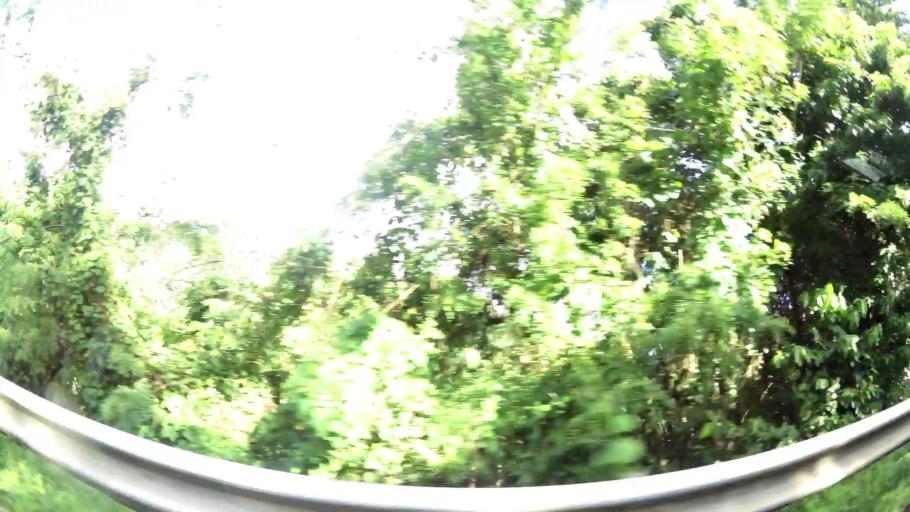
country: MQ
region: Martinique
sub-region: Martinique
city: Saint-Joseph
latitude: 14.6656
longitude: -61.0880
